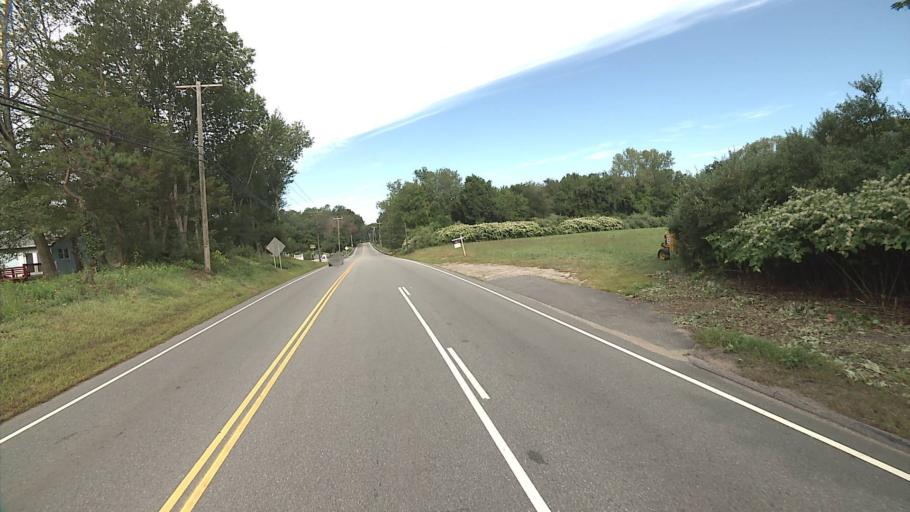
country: US
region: Connecticut
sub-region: Windham County
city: South Windham
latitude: 41.6187
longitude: -72.1499
